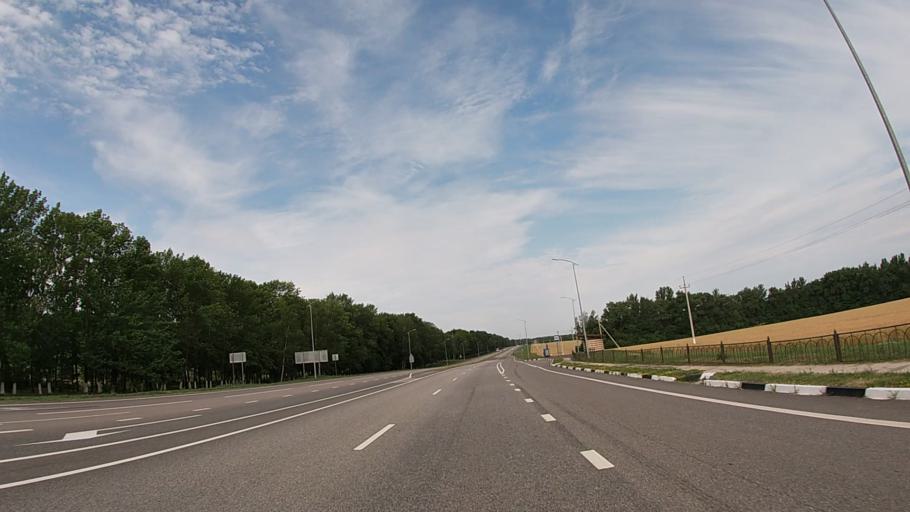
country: RU
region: Belgorod
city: Borisovka
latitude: 50.7522
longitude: 36.0155
